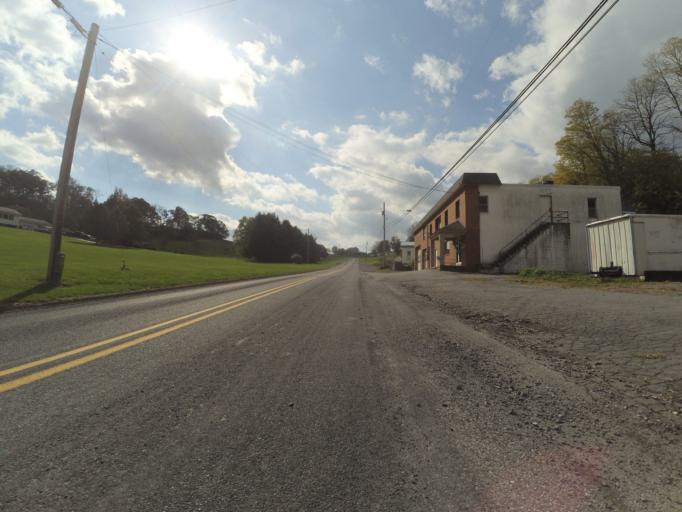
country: US
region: Pennsylvania
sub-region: Centre County
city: Bellefonte
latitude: 40.8920
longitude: -77.8032
